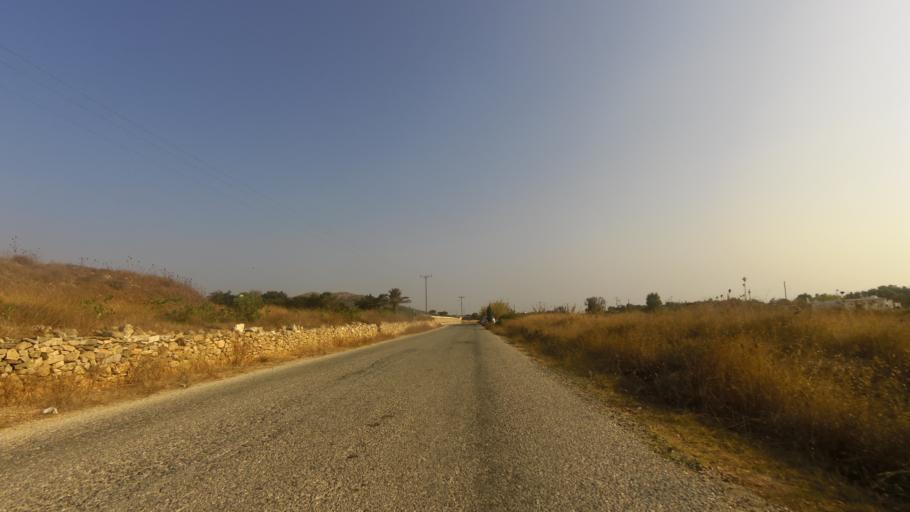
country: GR
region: South Aegean
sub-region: Nomos Kykladon
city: Antiparos
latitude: 37.0164
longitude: 25.0752
